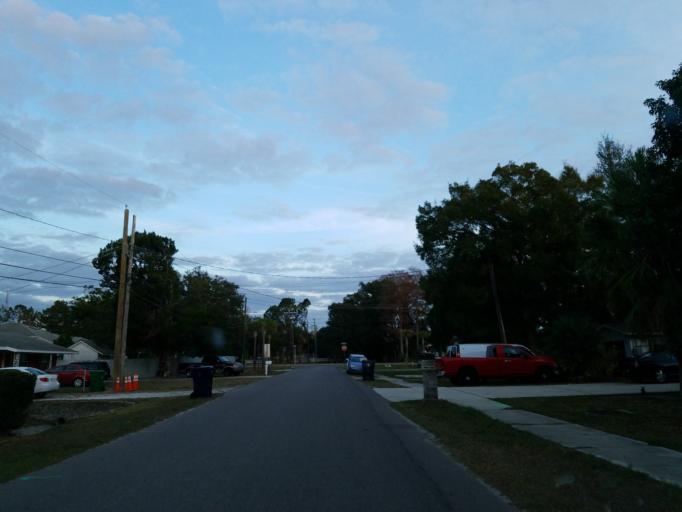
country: US
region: Florida
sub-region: Hillsborough County
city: Egypt Lake-Leto
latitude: 27.9776
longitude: -82.5147
